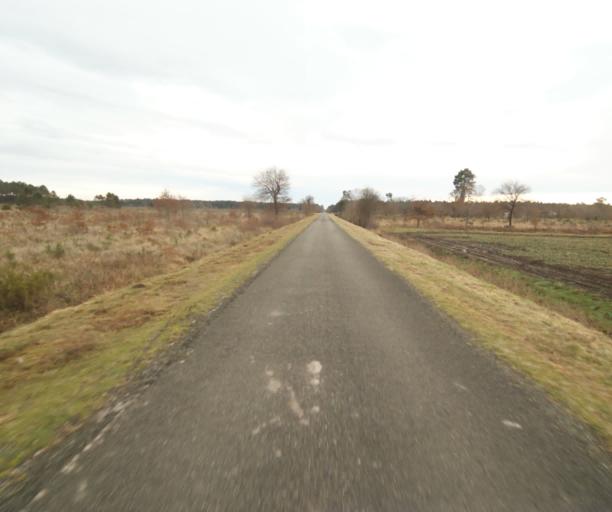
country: FR
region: Aquitaine
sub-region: Departement des Landes
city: Gabarret
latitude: 44.0297
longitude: -0.0594
